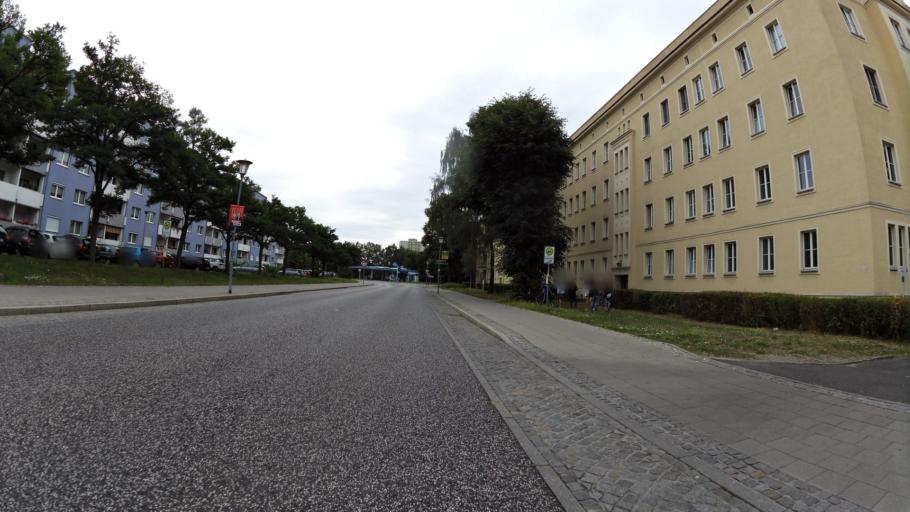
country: DE
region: Brandenburg
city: Eisenhuettenstadt
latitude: 52.1418
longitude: 14.6341
